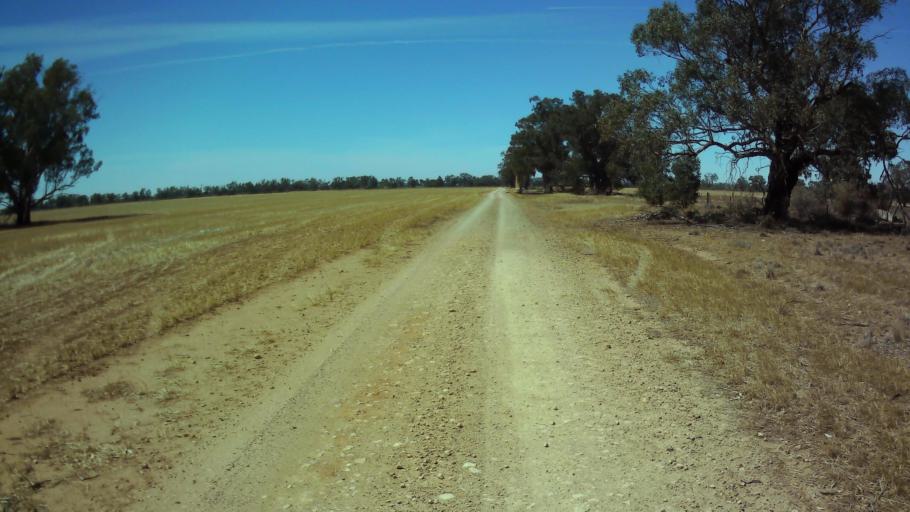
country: AU
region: New South Wales
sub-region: Weddin
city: Grenfell
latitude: -34.0307
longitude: 147.8905
